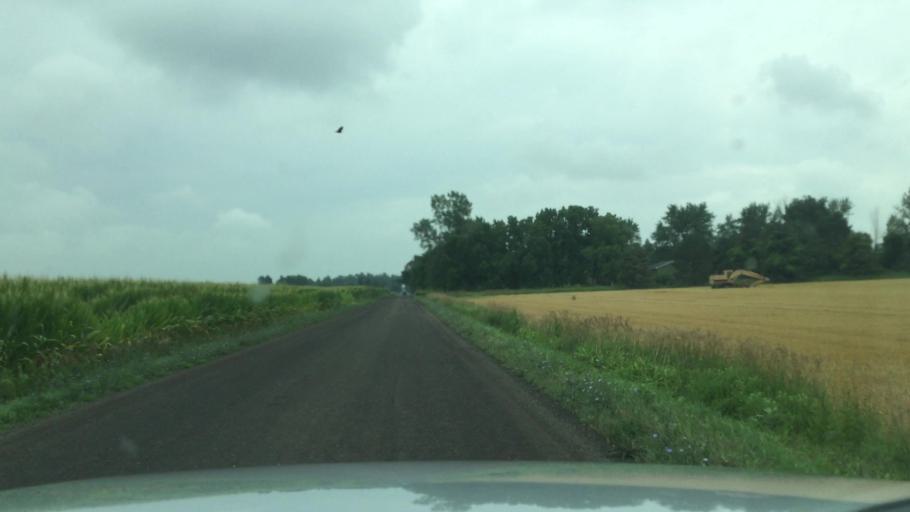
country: US
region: Michigan
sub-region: Shiawassee County
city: New Haven
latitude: 43.1151
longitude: -84.2261
